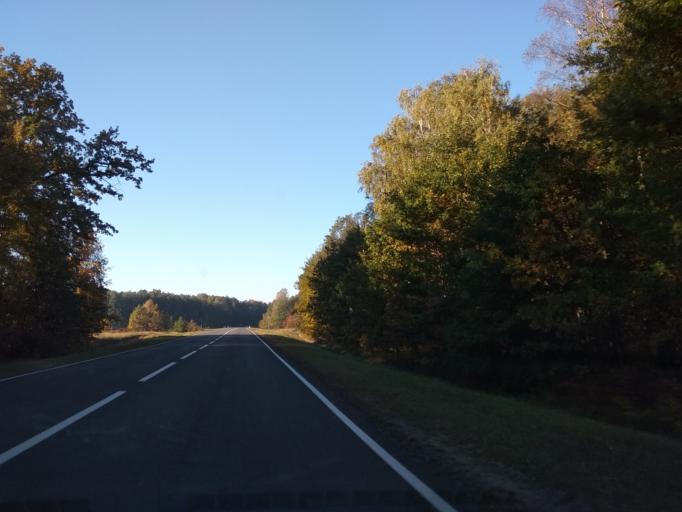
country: BY
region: Brest
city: Kobryn
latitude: 52.0157
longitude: 24.2355
